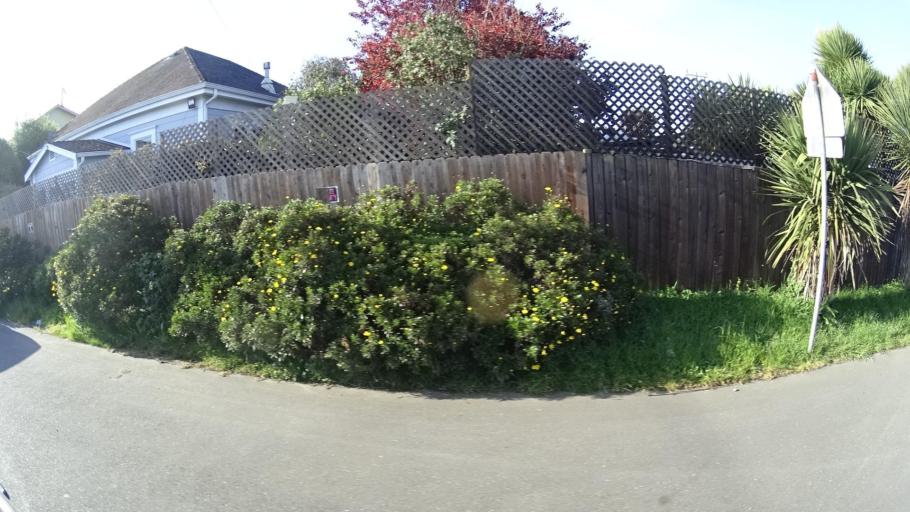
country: US
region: California
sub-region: Humboldt County
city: Bayview
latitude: 40.7732
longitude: -124.1809
